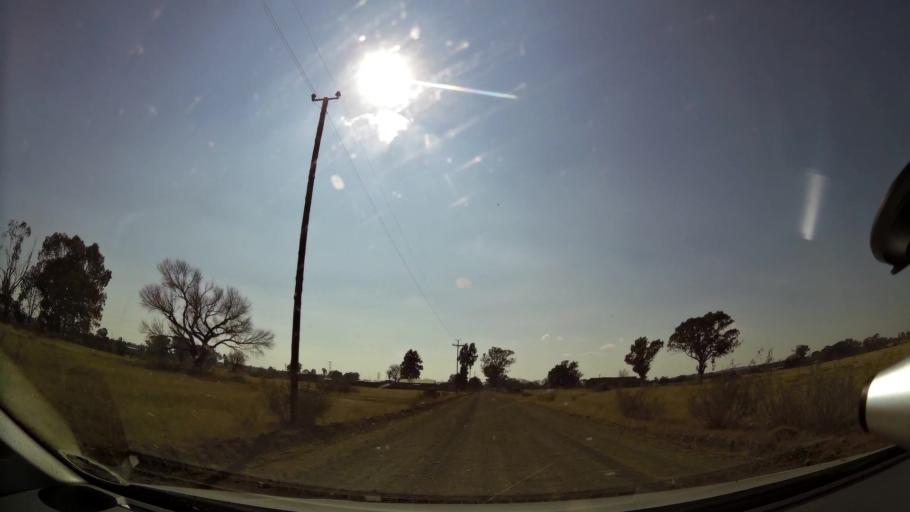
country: ZA
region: Orange Free State
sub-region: Mangaung Metropolitan Municipality
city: Bloemfontein
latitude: -29.1683
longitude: 26.3091
